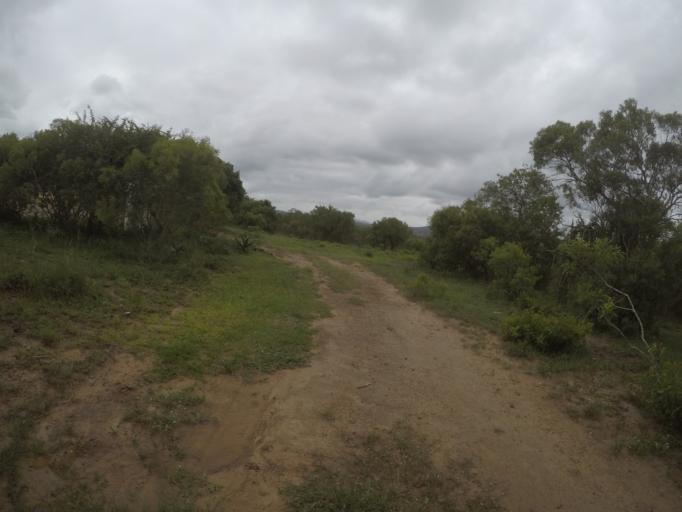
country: ZA
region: KwaZulu-Natal
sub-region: uThungulu District Municipality
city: Empangeni
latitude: -28.5922
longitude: 31.8465
